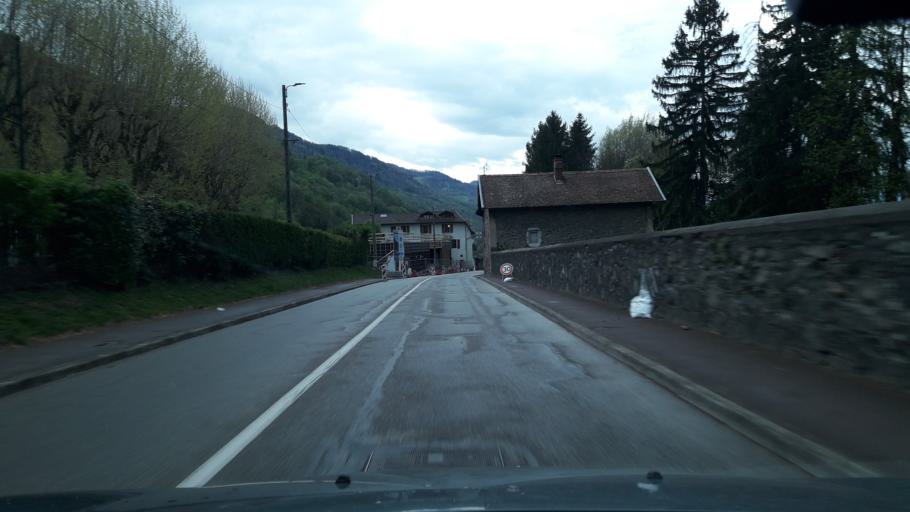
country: FR
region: Rhone-Alpes
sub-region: Departement de l'Isere
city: Villard-Bonnot
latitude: 45.2458
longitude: 5.8953
